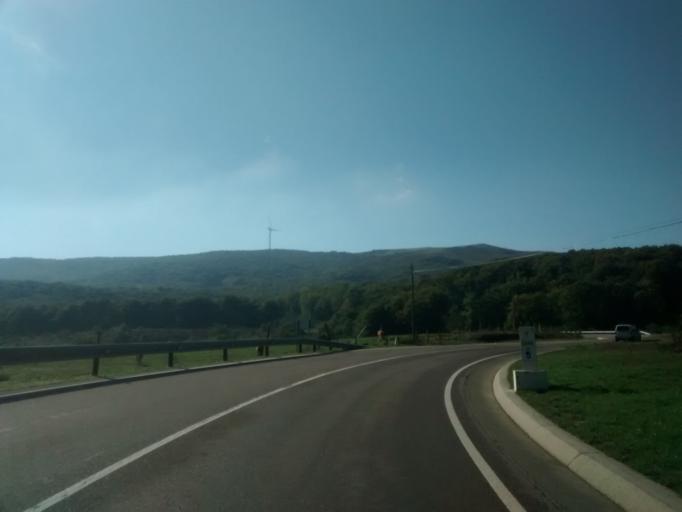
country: ES
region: Cantabria
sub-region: Provincia de Cantabria
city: Reinosa
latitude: 42.9779
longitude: -4.1024
